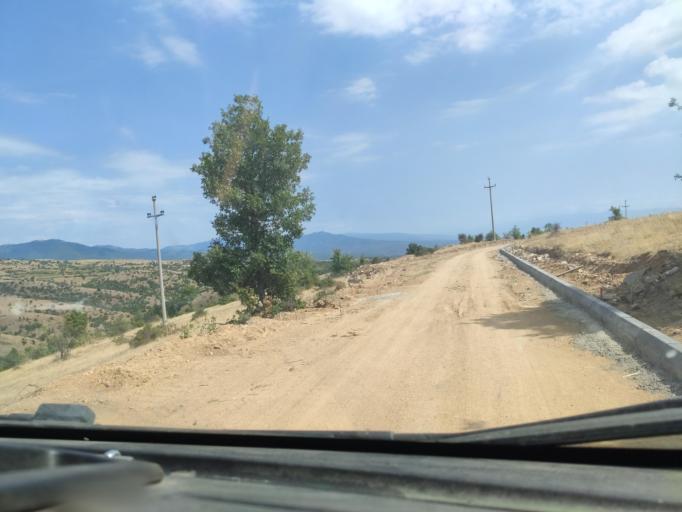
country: MK
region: Radovis
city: Radovish
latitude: 41.6684
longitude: 22.4056
